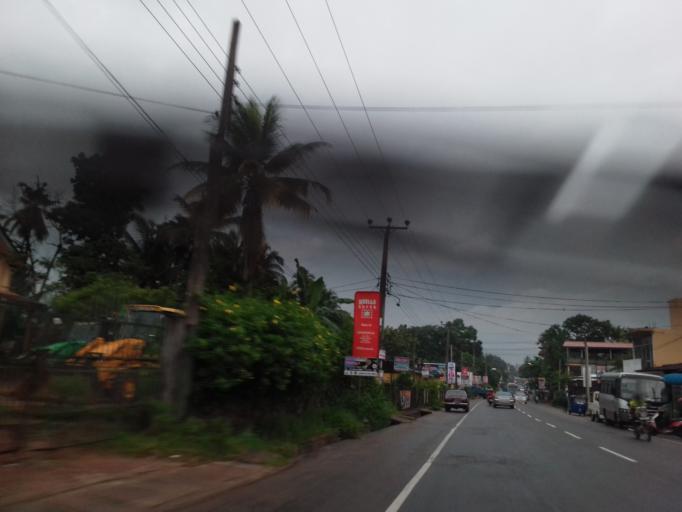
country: LK
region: Western
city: Battaramulla South
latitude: 6.8938
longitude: 79.9621
